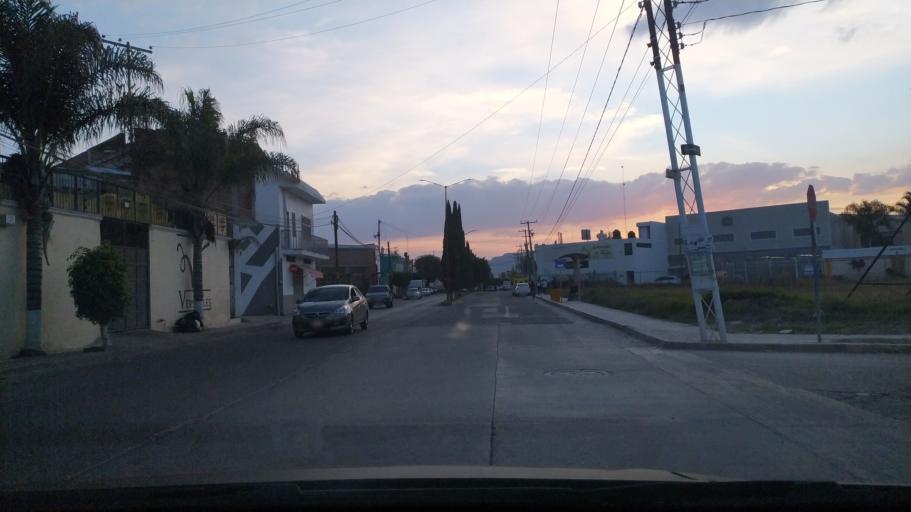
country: MX
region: Guanajuato
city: San Francisco del Rincon
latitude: 21.0304
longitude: -101.8515
